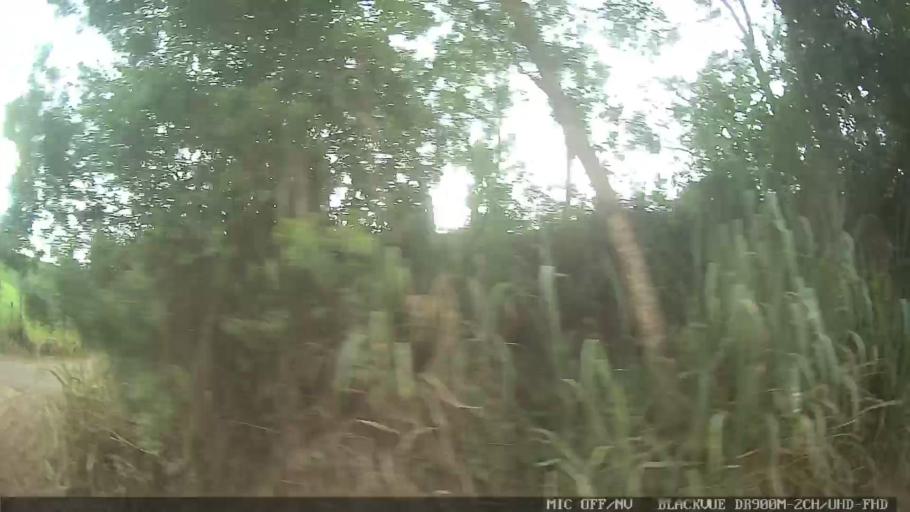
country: BR
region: Sao Paulo
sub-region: Bom Jesus Dos Perdoes
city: Bom Jesus dos Perdoes
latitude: -23.1232
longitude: -46.5000
